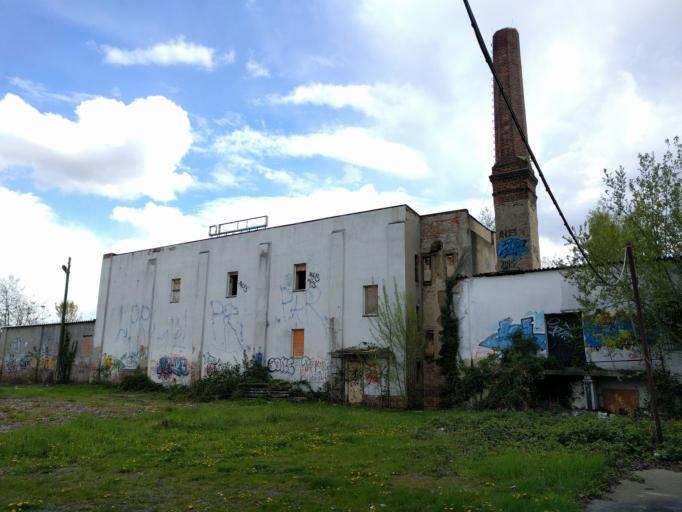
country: DE
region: Saxony
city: Dresden
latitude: 51.0546
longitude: 13.7661
